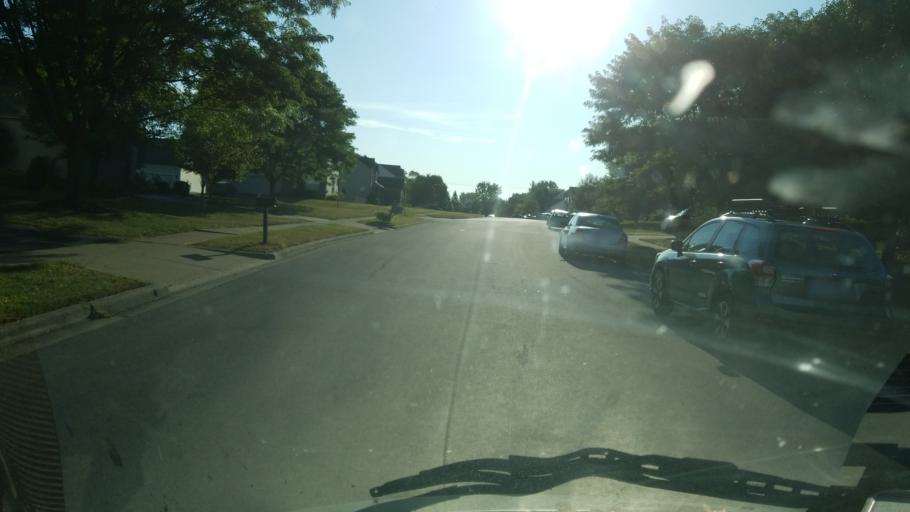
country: US
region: Ohio
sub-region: Delaware County
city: Lewis Center
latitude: 40.1654
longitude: -82.9959
